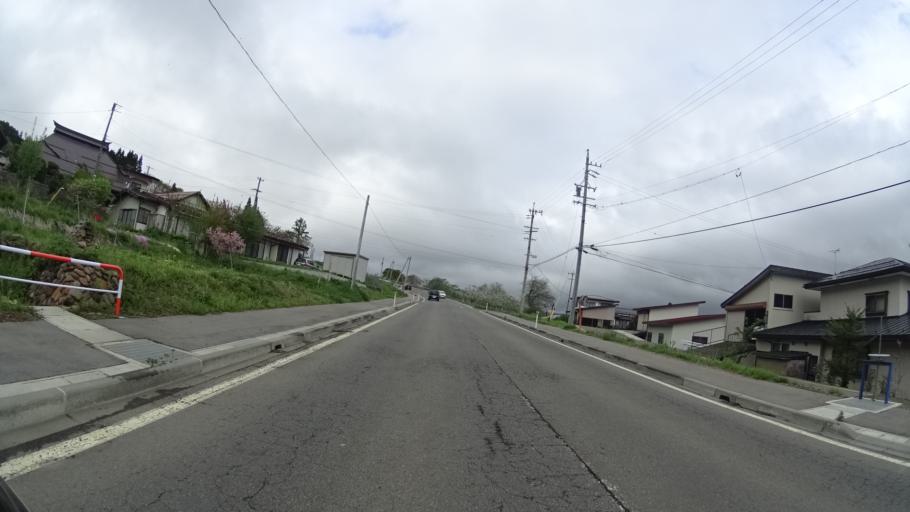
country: JP
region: Nagano
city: Nagano-shi
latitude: 36.7394
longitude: 138.2054
